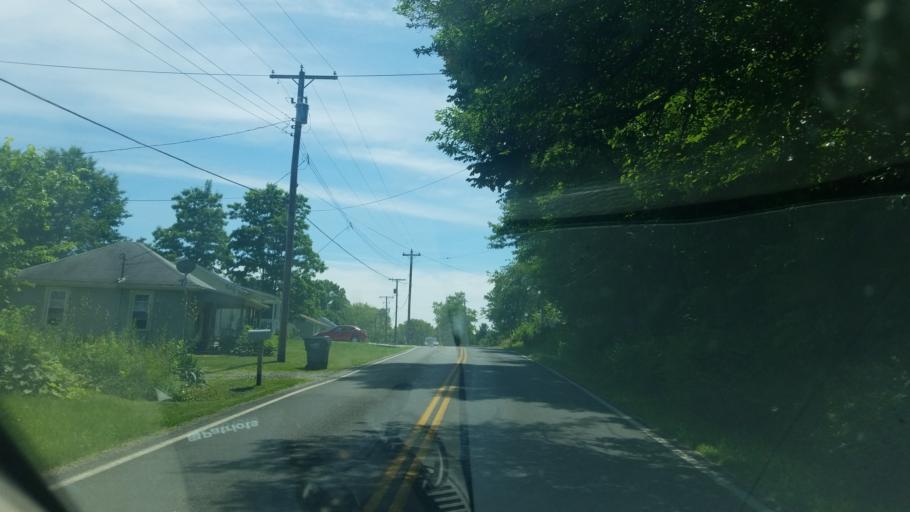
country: US
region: Ohio
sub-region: Stark County
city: Louisville
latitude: 40.8423
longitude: -81.2351
